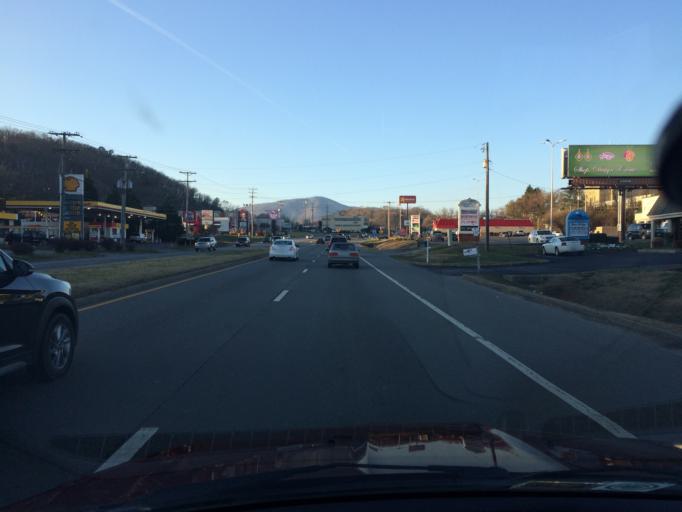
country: US
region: Virginia
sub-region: Roanoke County
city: Narrows
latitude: 37.2263
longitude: -79.9808
